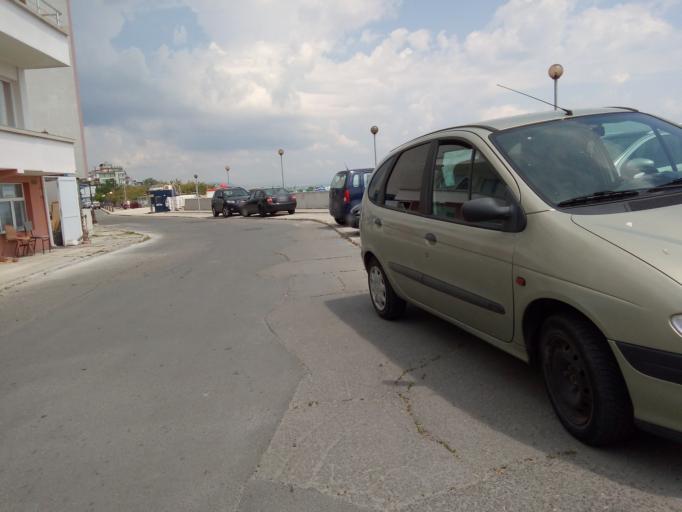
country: BG
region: Burgas
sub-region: Obshtina Pomorie
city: Pomorie
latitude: 42.5588
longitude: 27.6460
